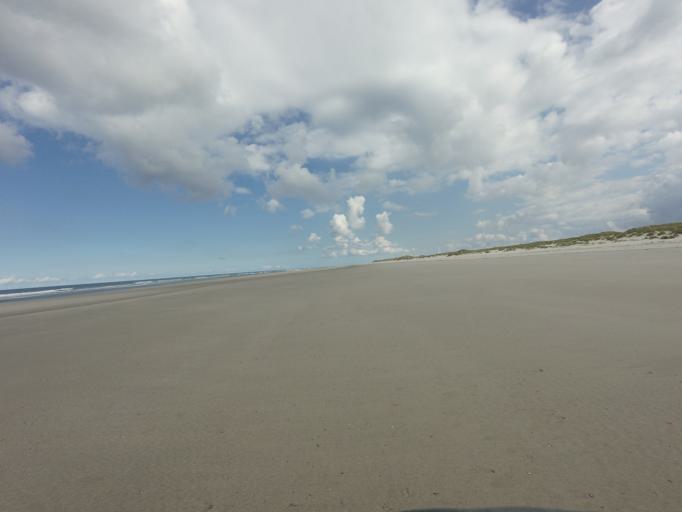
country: NL
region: Friesland
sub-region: Gemeente Terschelling
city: West-Terschelling
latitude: 53.3940
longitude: 5.2014
